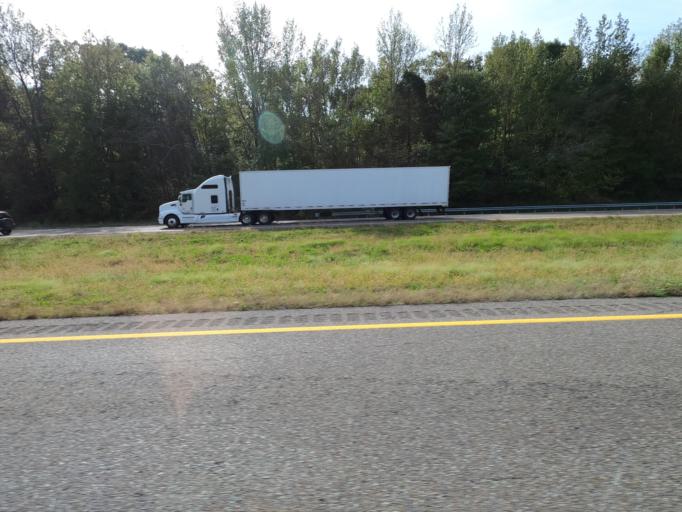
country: US
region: Tennessee
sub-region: Humphreys County
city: New Johnsonville
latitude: 35.8687
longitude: -87.8739
